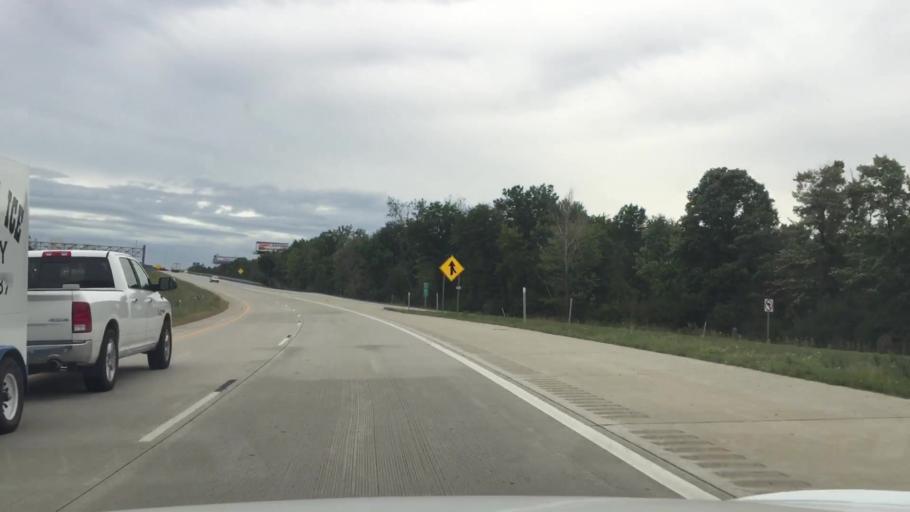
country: US
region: Michigan
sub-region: Saint Clair County
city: Marysville
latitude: 42.9699
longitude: -82.4899
